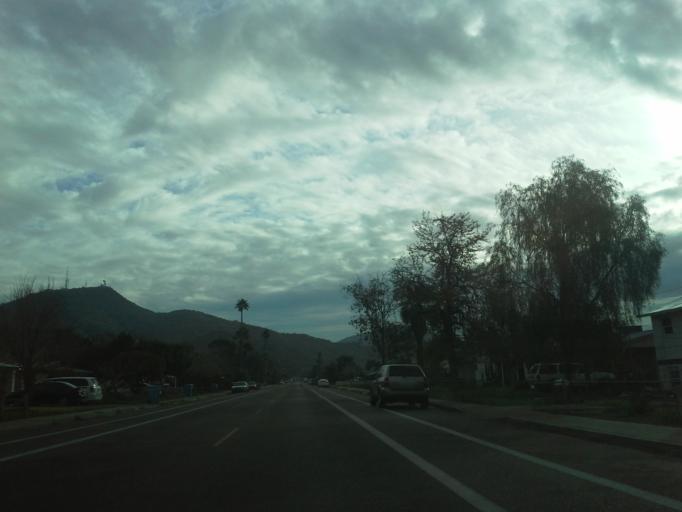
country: US
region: Arizona
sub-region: Maricopa County
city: Glendale
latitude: 33.5892
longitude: -112.1055
